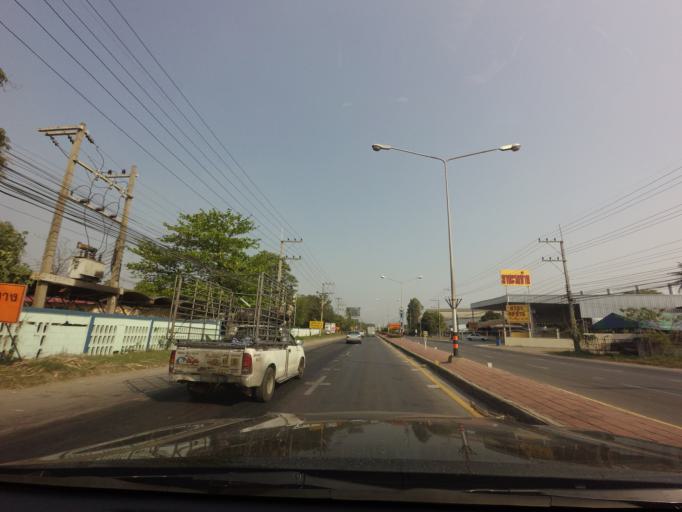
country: TH
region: Kanchanaburi
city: Tha Maka
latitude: 13.8994
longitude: 99.7911
